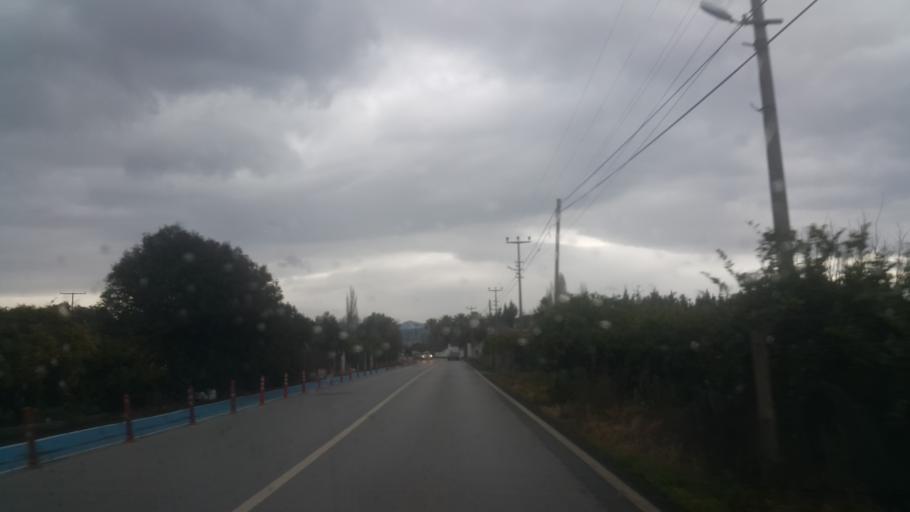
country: TR
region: Izmir
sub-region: Seferihisar
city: Seferhisar
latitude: 38.1910
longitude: 26.8188
